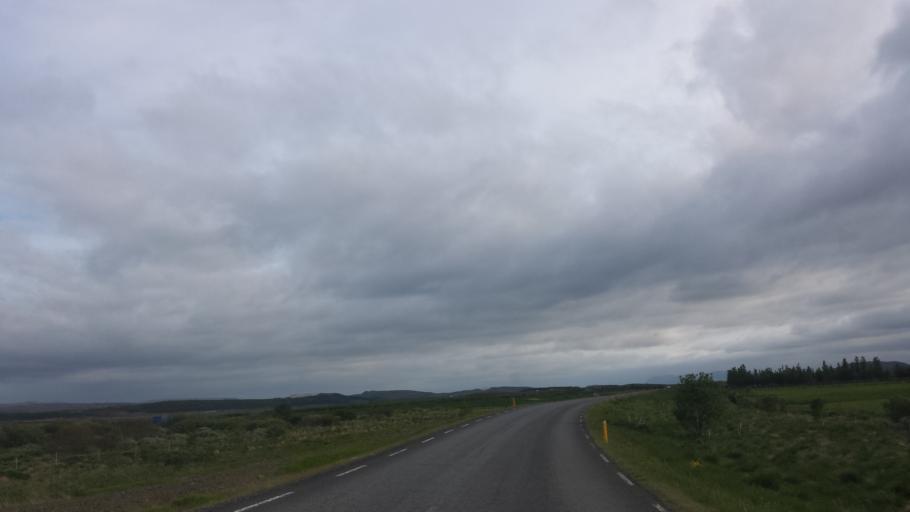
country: IS
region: South
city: Selfoss
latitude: 64.2497
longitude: -20.3223
